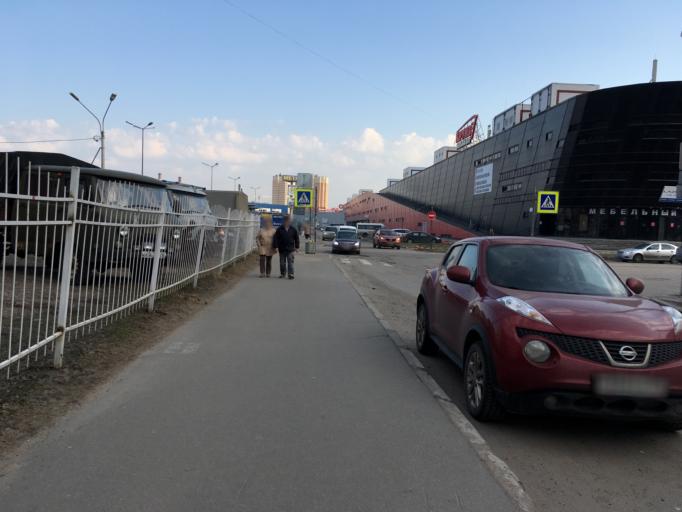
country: RU
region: St.-Petersburg
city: Komendantsky aerodrom
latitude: 60.0039
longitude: 30.2648
